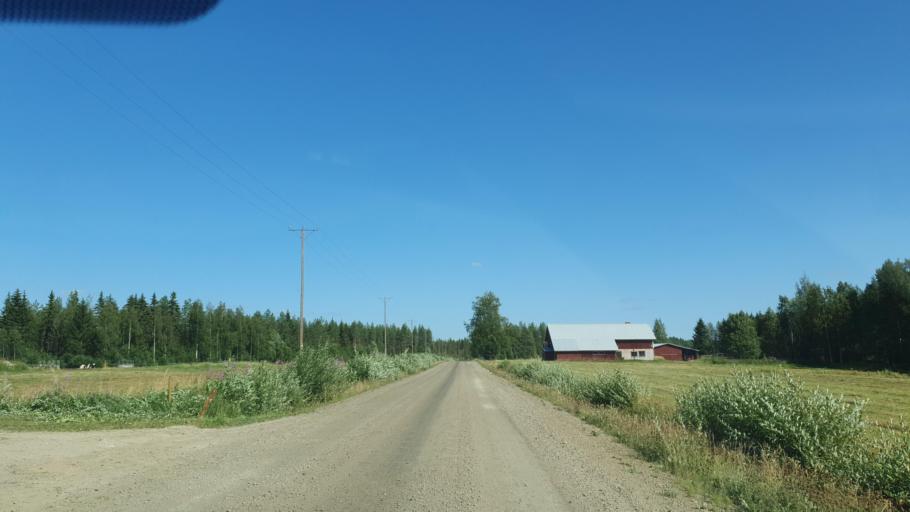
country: FI
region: Kainuu
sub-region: Kehys-Kainuu
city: Kuhmo
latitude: 64.0523
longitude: 29.5902
